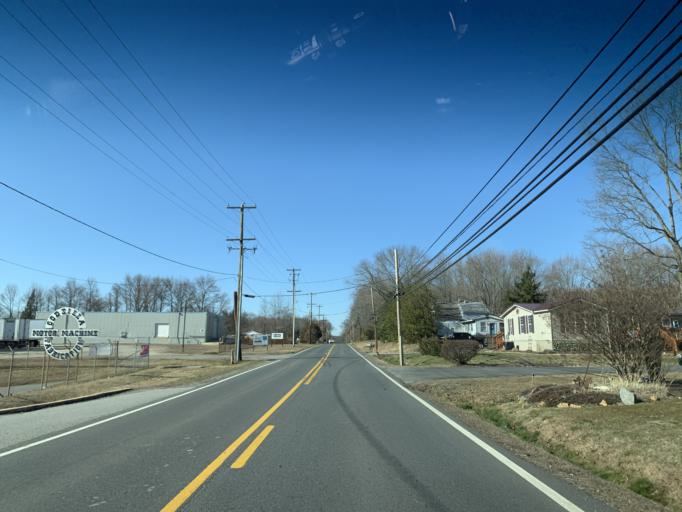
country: US
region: Maryland
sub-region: Cecil County
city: Elkton
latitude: 39.6229
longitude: -75.8527
